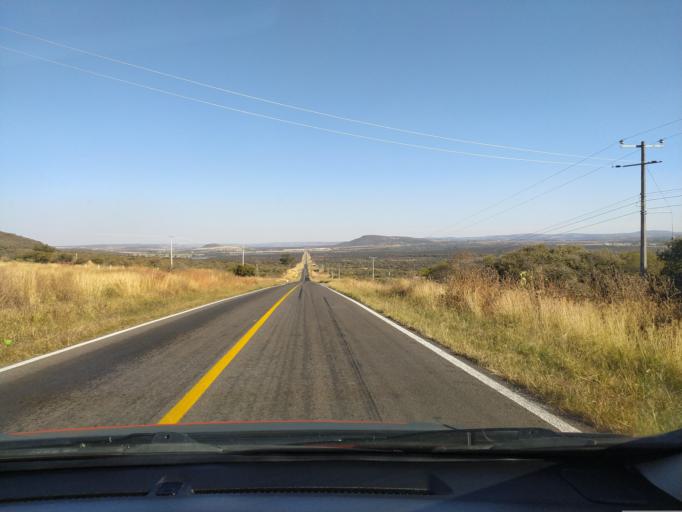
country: MX
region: Jalisco
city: Valle de Guadalupe
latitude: 21.0186
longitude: -102.5203
